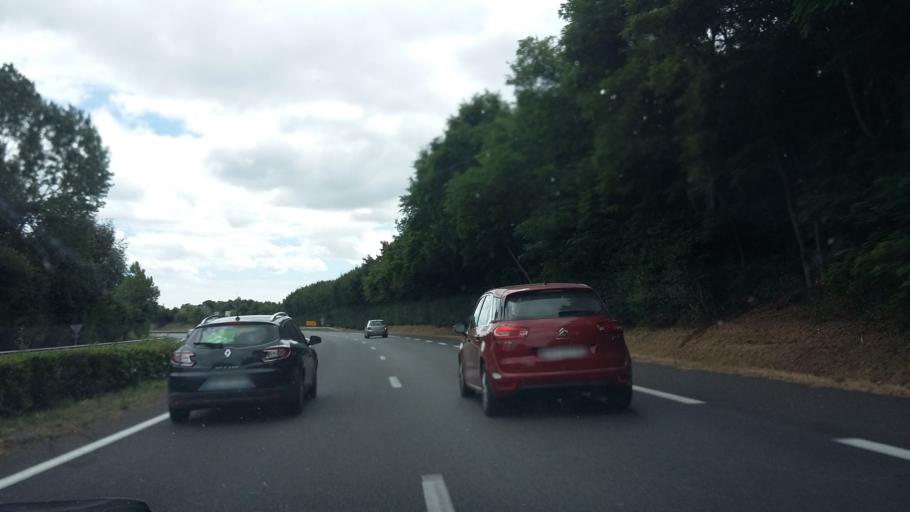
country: FR
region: Pays de la Loire
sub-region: Departement de la Vendee
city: Challans
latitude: 46.8442
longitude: -1.8527
